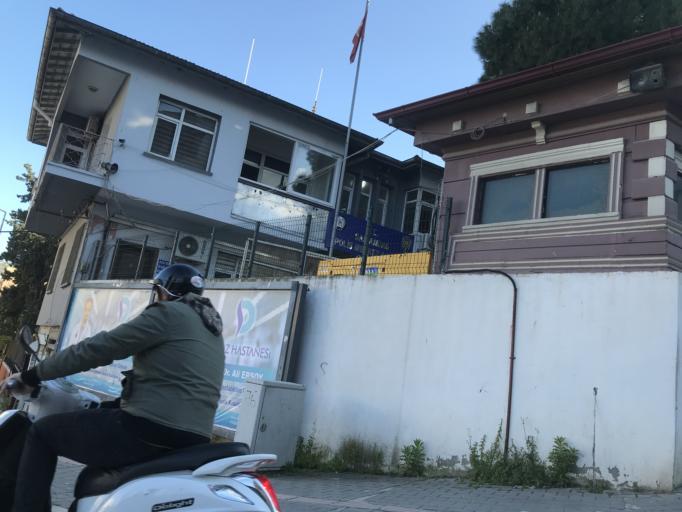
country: TR
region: Hatay
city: Samandag
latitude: 36.0838
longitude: 35.9826
